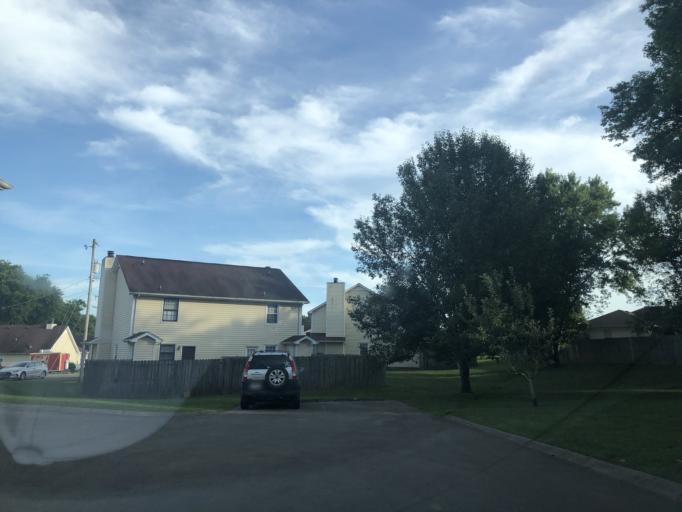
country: US
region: Tennessee
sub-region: Davidson County
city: Belle Meade
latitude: 36.0705
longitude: -86.9392
